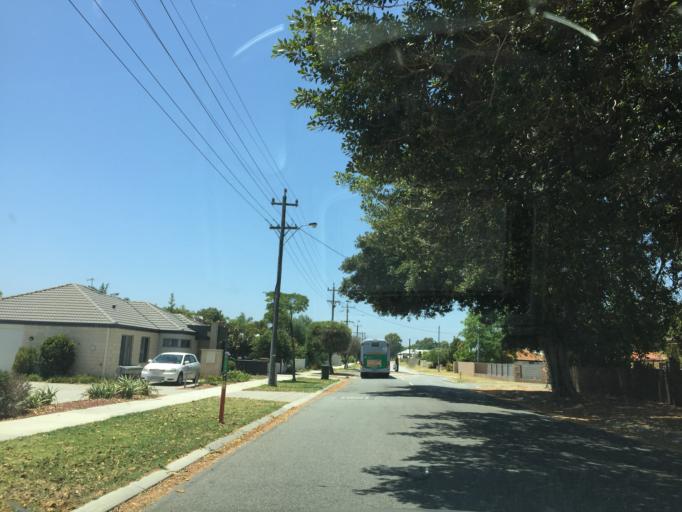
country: AU
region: Western Australia
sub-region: Canning
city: Queens Park
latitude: -32.0100
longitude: 115.9443
